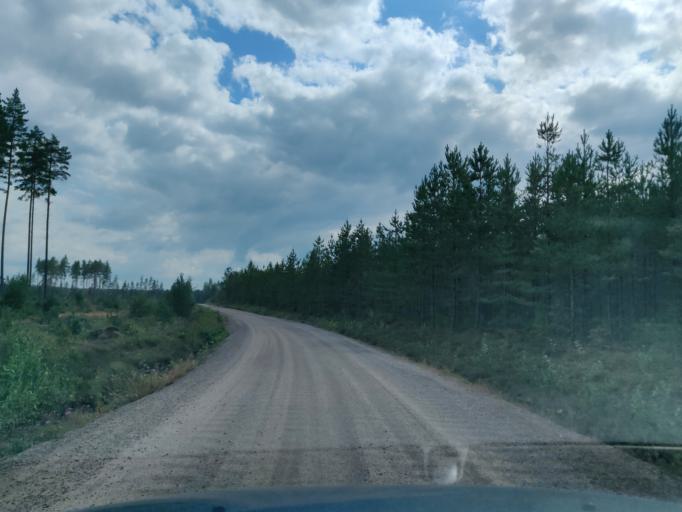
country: SE
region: Vaermland
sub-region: Hagfors Kommun
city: Hagfors
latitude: 59.9794
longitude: 13.5486
